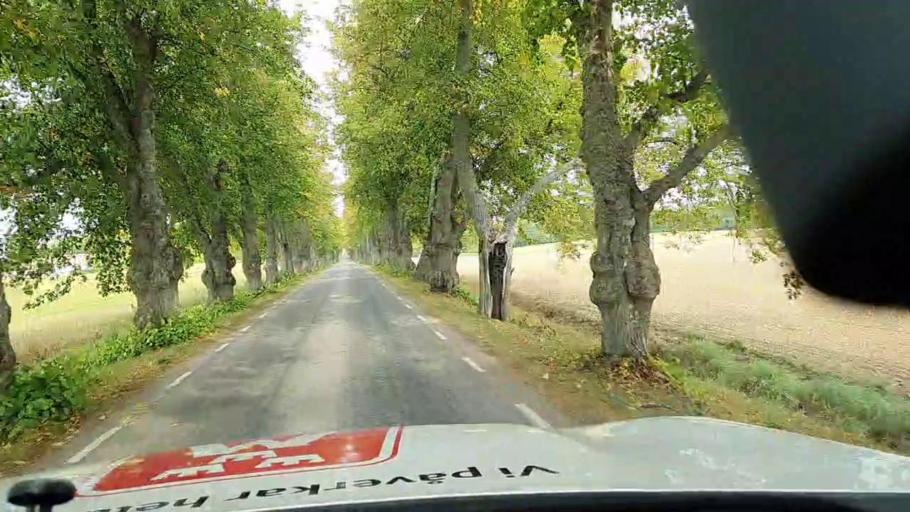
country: SE
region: Soedermanland
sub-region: Nykopings Kommun
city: Svalsta
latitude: 58.8200
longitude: 16.8946
